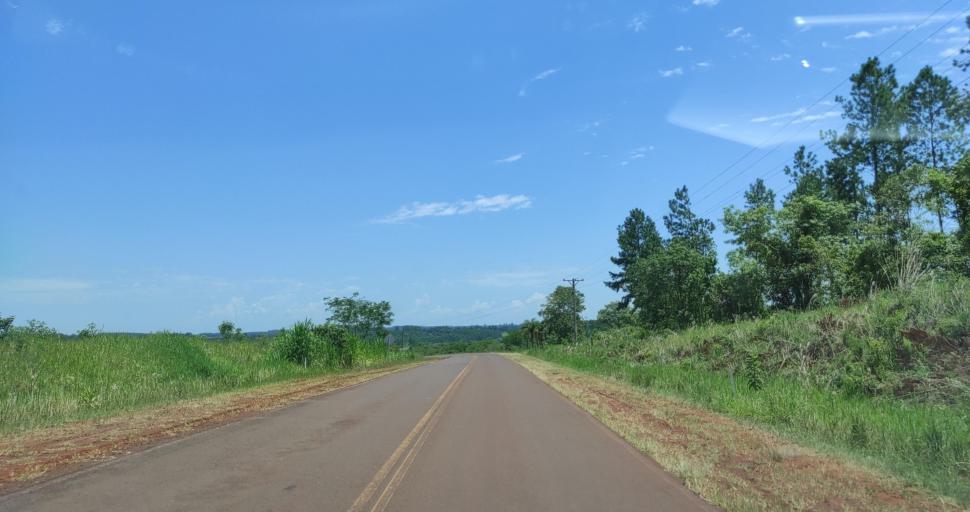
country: AR
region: Misiones
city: Ruiz de Montoya
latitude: -27.0214
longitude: -55.0339
